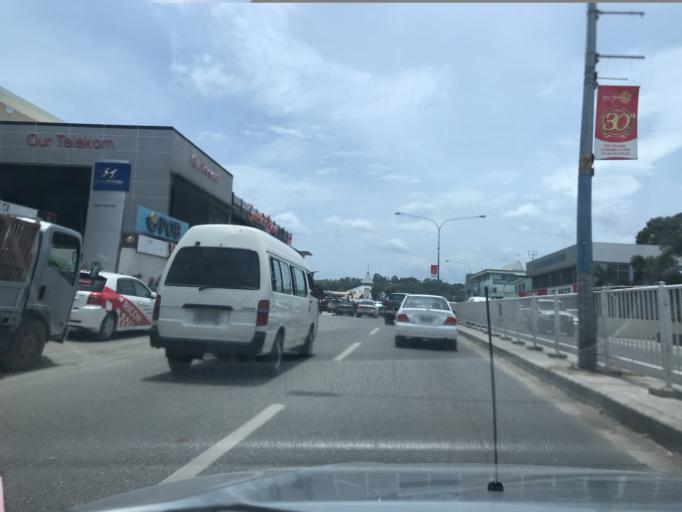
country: SB
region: Guadalcanal
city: Honiara
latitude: -9.4329
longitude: 159.9603
